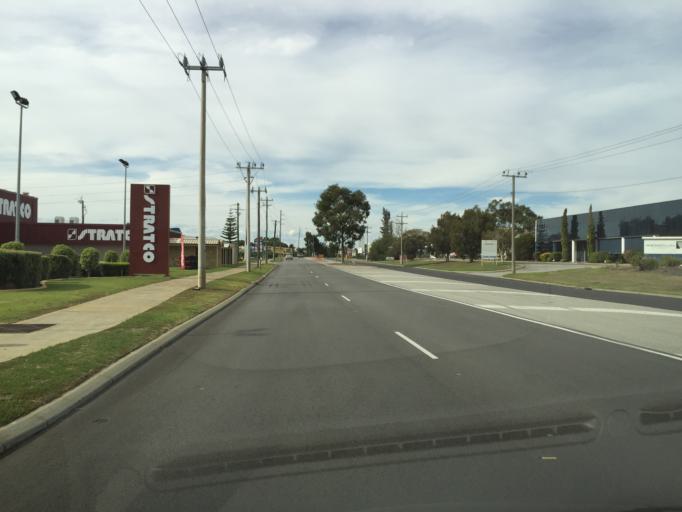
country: AU
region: Western Australia
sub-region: Canning
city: Canning Vale
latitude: -32.0622
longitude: 115.9045
